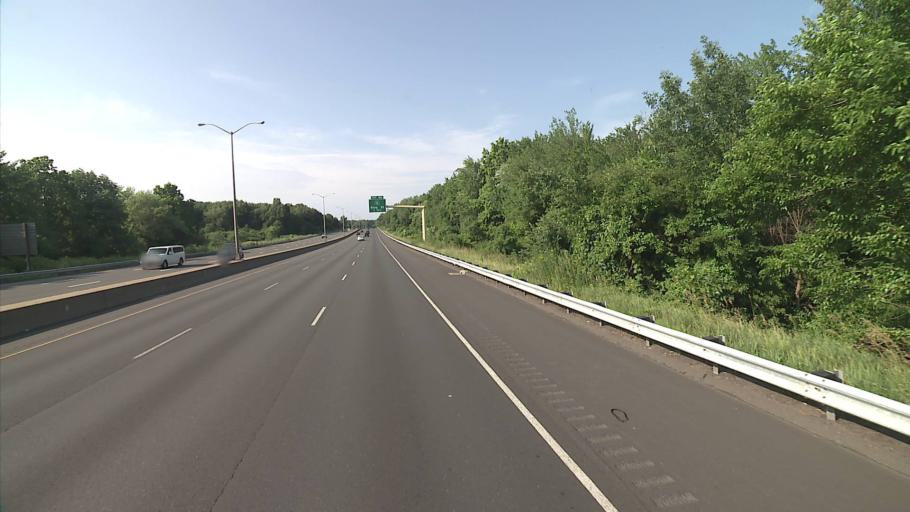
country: US
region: Connecticut
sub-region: Hartford County
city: Enfield
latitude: 41.9681
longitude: -72.5891
